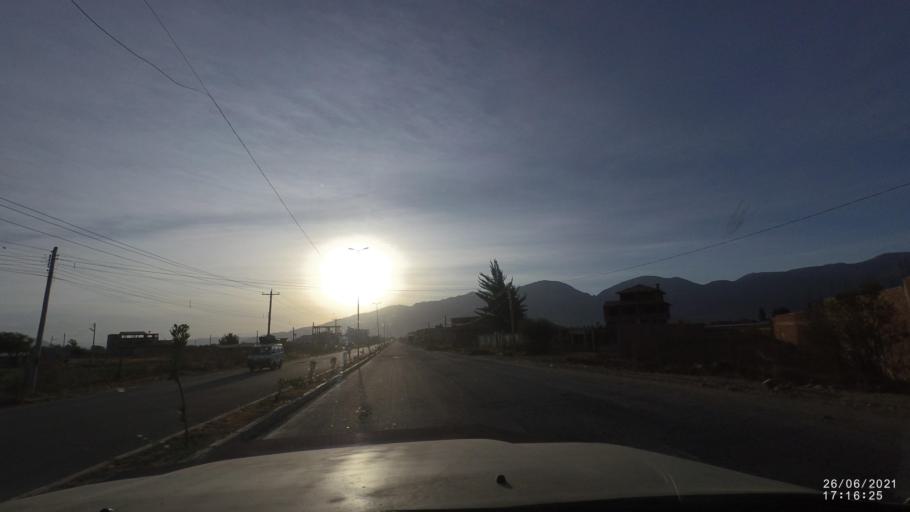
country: BO
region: Cochabamba
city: Cliza
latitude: -17.5592
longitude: -65.9376
